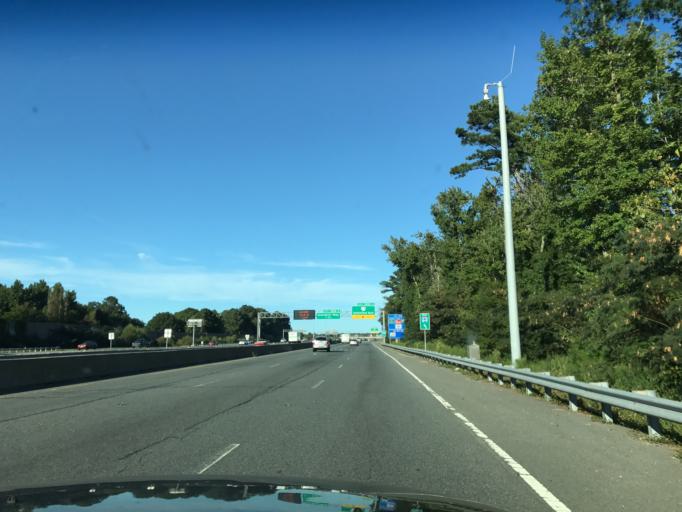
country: US
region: Virginia
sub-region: City of Chesapeake
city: Chesapeake
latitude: 36.7657
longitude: -76.2641
